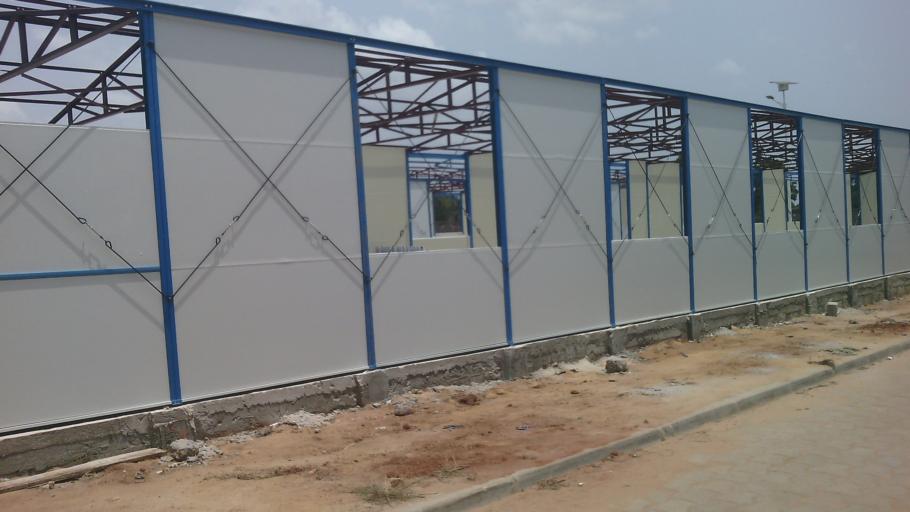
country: BJ
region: Atlantique
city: Abomey-Calavi
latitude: 6.4215
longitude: 2.3398
